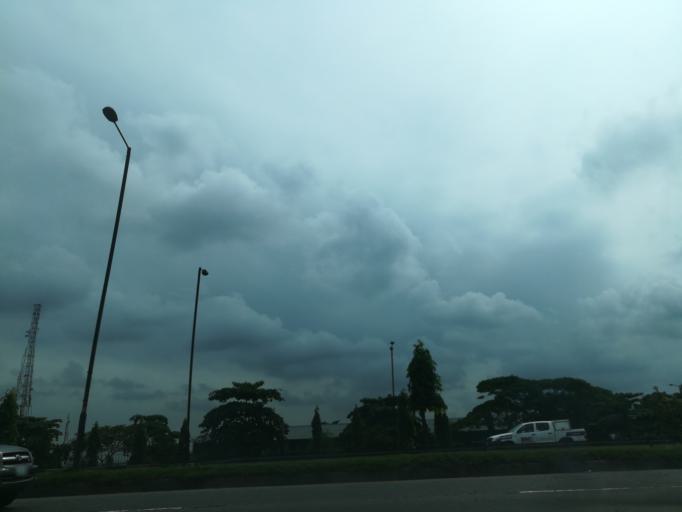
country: NG
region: Lagos
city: Ojota
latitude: 6.5952
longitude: 3.3814
